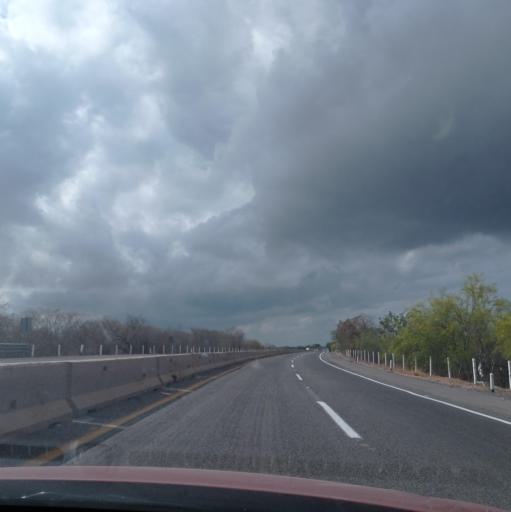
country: MX
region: Sinaloa
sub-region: Navolato
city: Juan Aldama (El Tigre)
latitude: 24.9900
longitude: -107.7725
